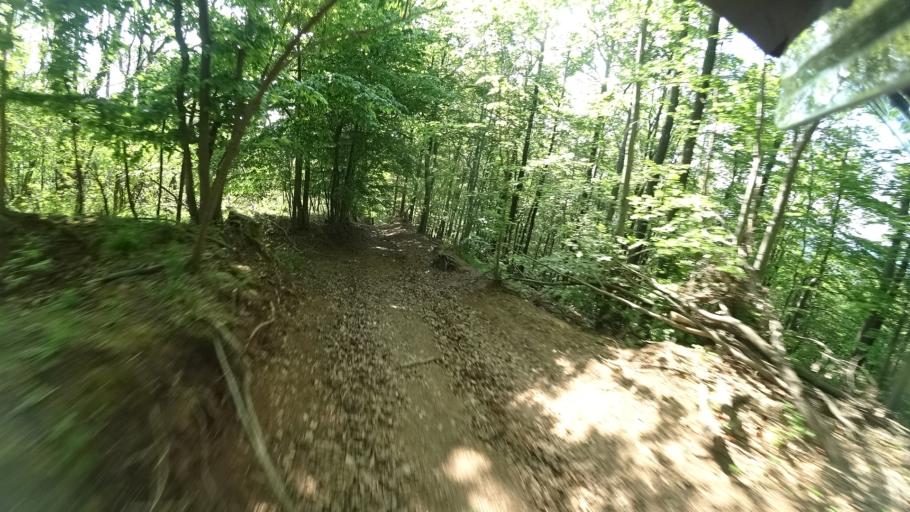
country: HR
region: Zagrebacka
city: Jablanovec
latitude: 45.8962
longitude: 15.8961
